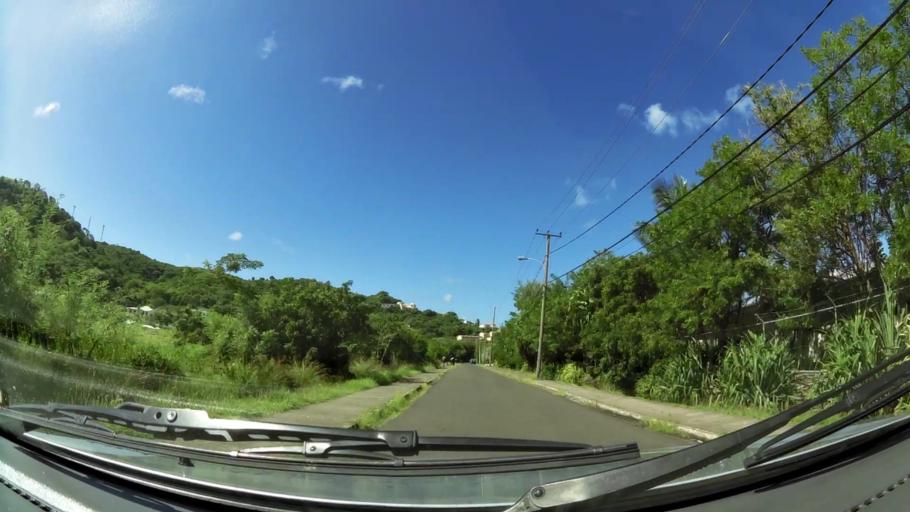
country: GD
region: Saint George
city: Saint George's
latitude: 12.0219
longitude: -61.7638
